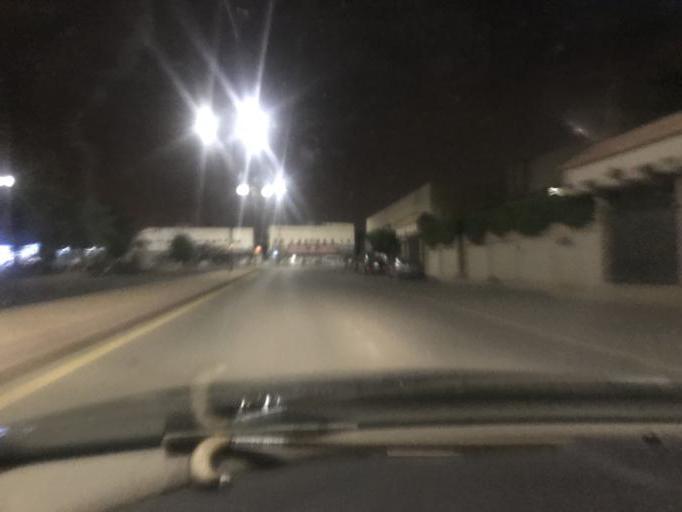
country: SA
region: Ar Riyad
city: Riyadh
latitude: 24.7328
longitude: 46.7763
